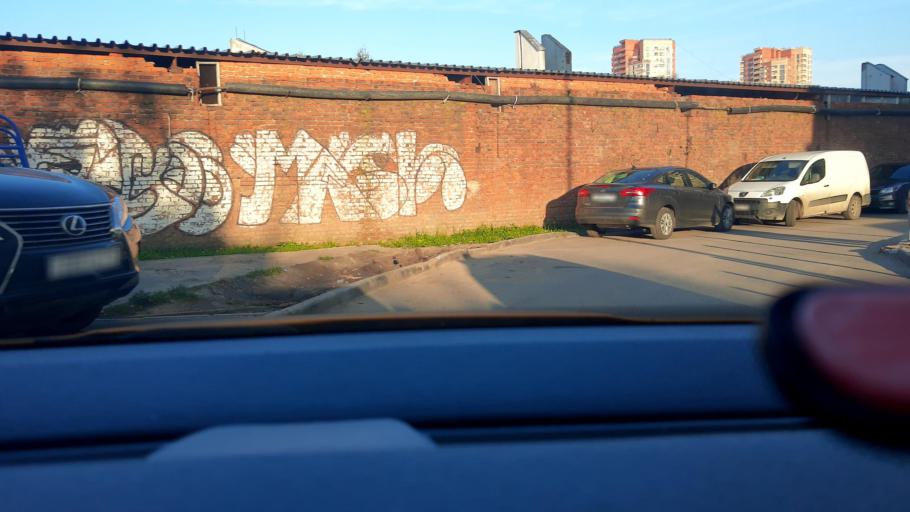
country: RU
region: Moskovskaya
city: Levoberezhnaya
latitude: 55.8724
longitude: 37.4784
